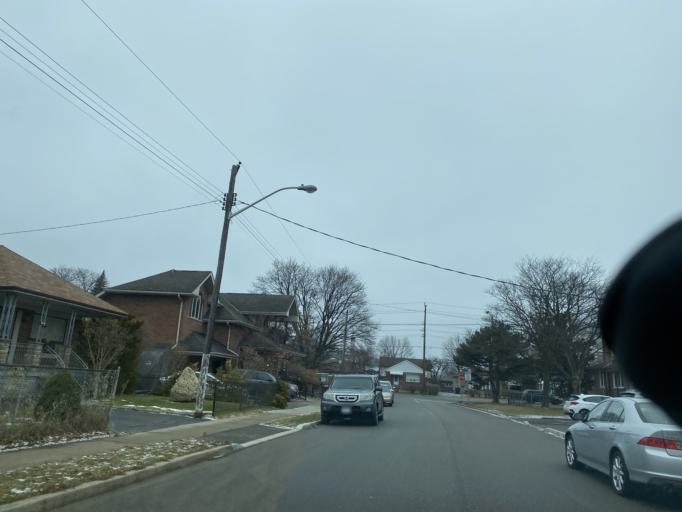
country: CA
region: Ontario
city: Scarborough
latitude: 43.7602
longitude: -79.3086
